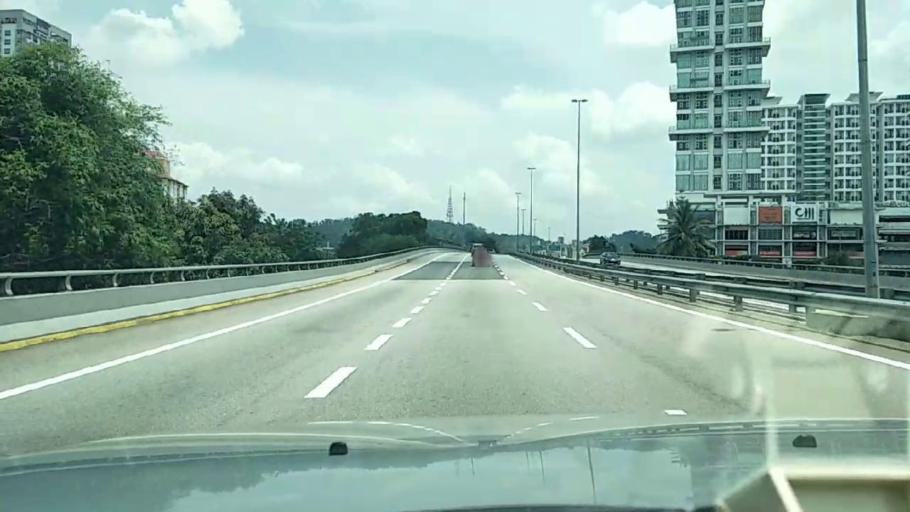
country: MY
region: Kuala Lumpur
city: Kuala Lumpur
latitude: 3.0939
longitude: 101.6768
